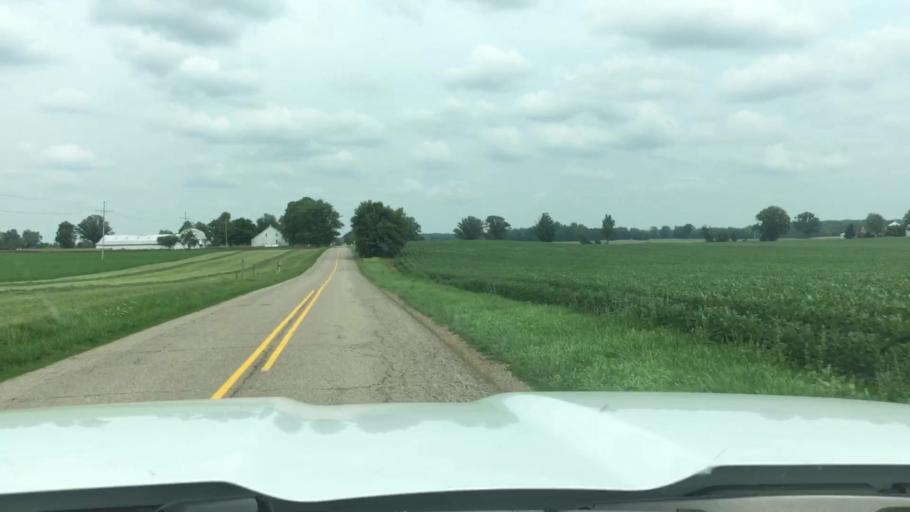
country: US
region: Michigan
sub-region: Ingham County
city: Webberville
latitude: 42.7096
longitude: -84.1917
